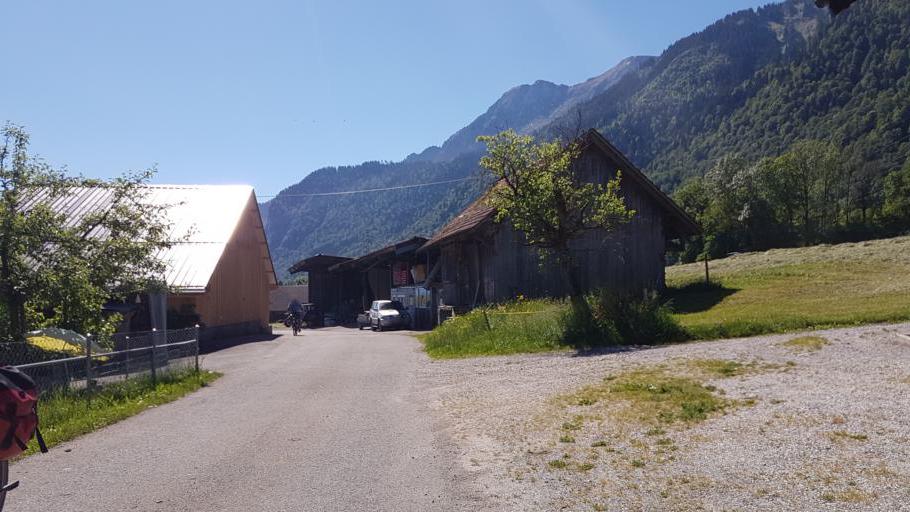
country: CH
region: Bern
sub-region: Thun District
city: Blumenstein
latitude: 46.7227
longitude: 7.5399
